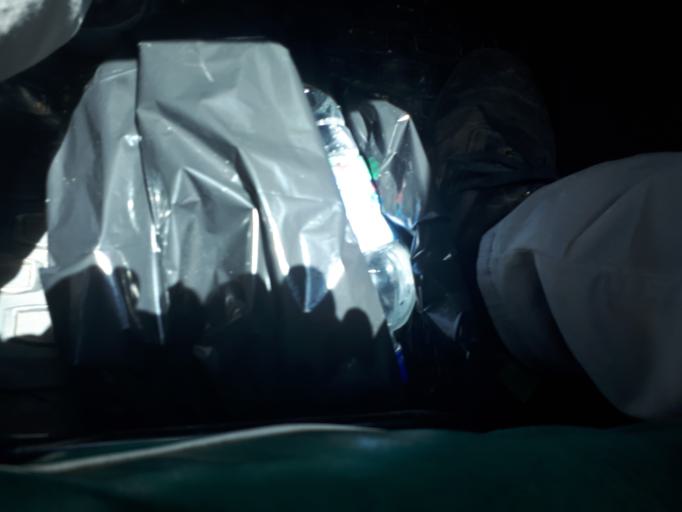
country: VU
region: Sanma
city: Luganville
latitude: -15.5783
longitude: 167.1222
